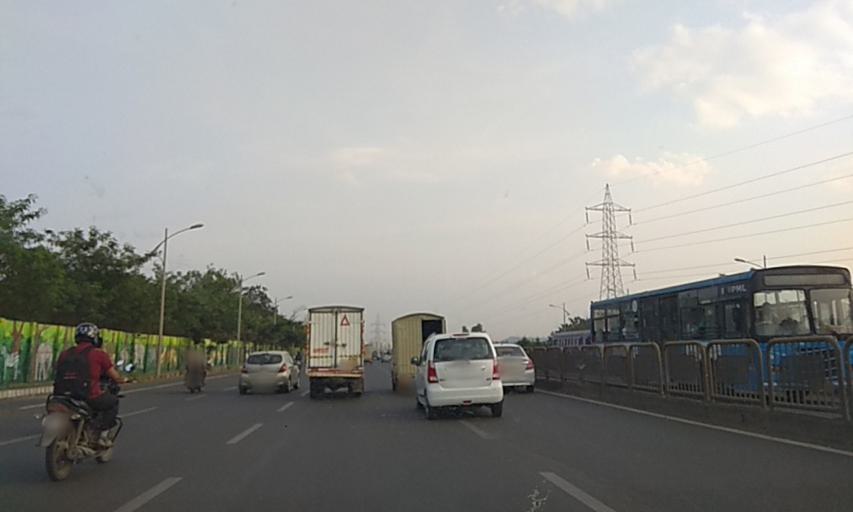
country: IN
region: Maharashtra
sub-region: Pune Division
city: Pimpri
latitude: 18.5805
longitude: 73.7995
